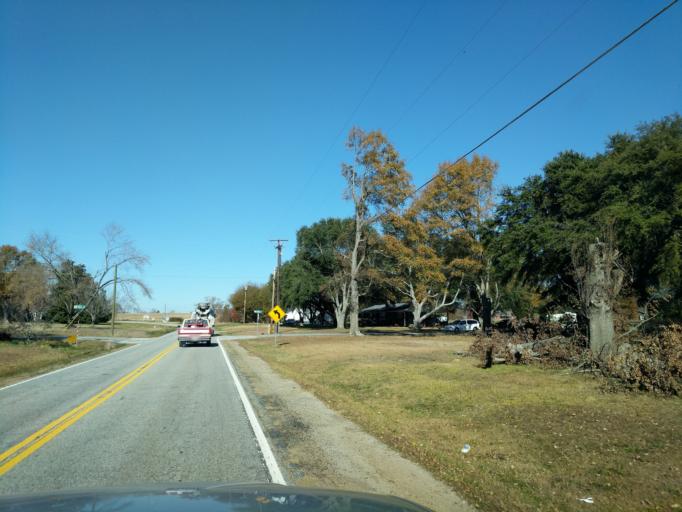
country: US
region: South Carolina
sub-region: Spartanburg County
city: Duncan
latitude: 35.0050
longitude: -82.1758
